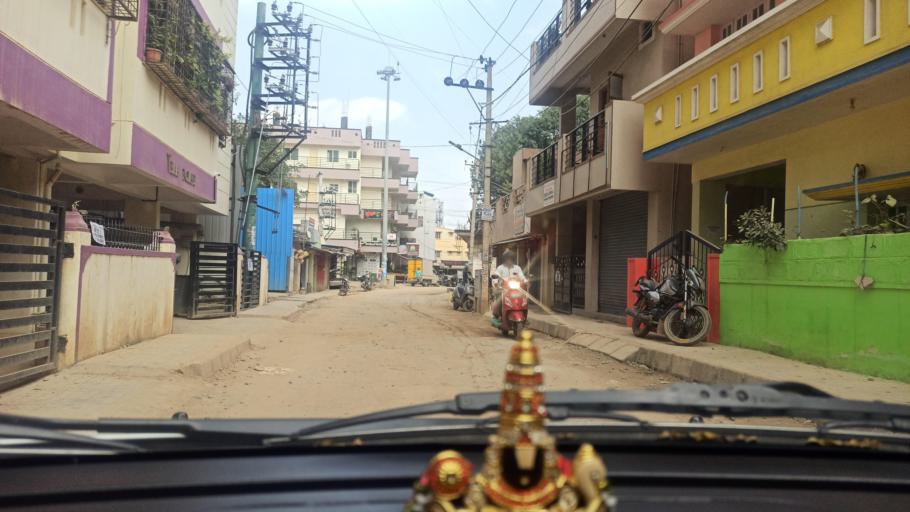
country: IN
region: Karnataka
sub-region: Bangalore Urban
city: Bangalore
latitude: 13.0190
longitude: 77.6656
